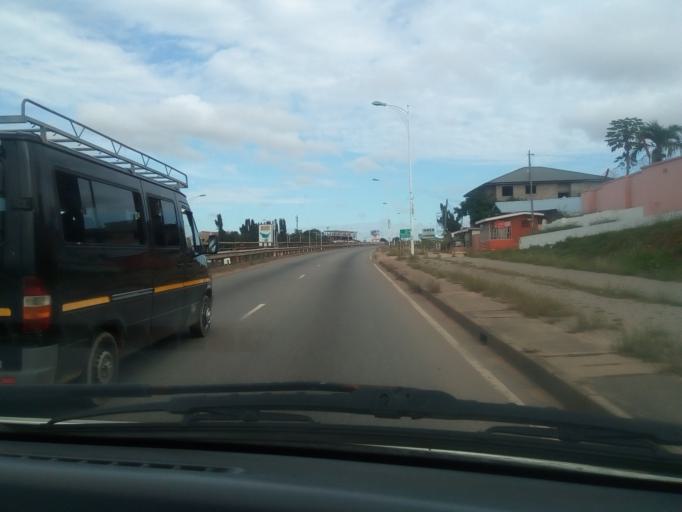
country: GH
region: Greater Accra
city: Dome
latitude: 5.6471
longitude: -0.2492
